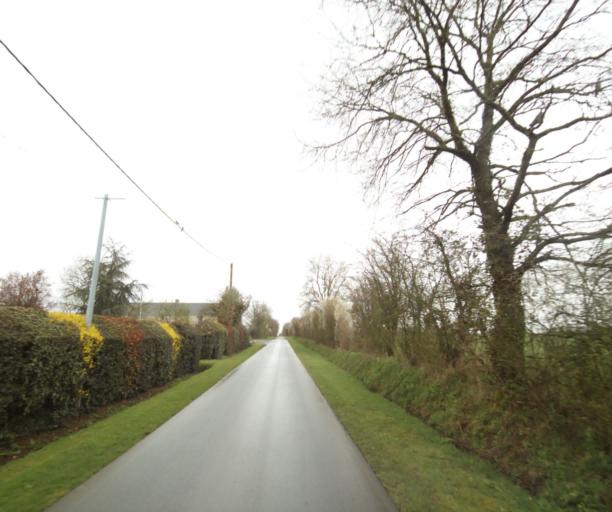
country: FR
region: Pays de la Loire
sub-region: Departement de la Loire-Atlantique
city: Bouvron
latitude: 47.4464
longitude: -1.8782
